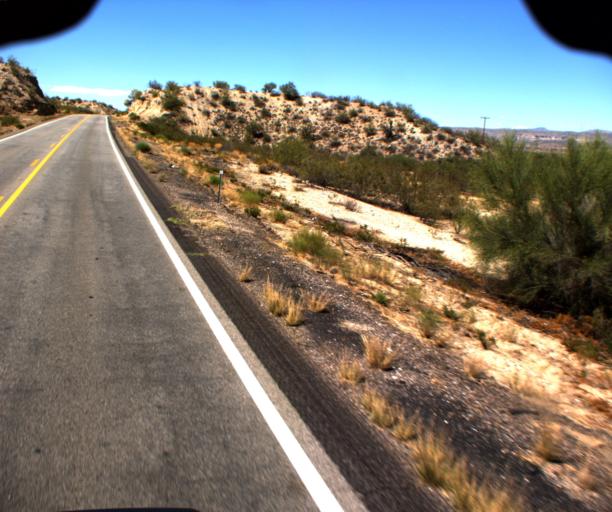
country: US
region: Arizona
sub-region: Yavapai County
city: Bagdad
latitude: 34.7754
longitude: -113.6219
